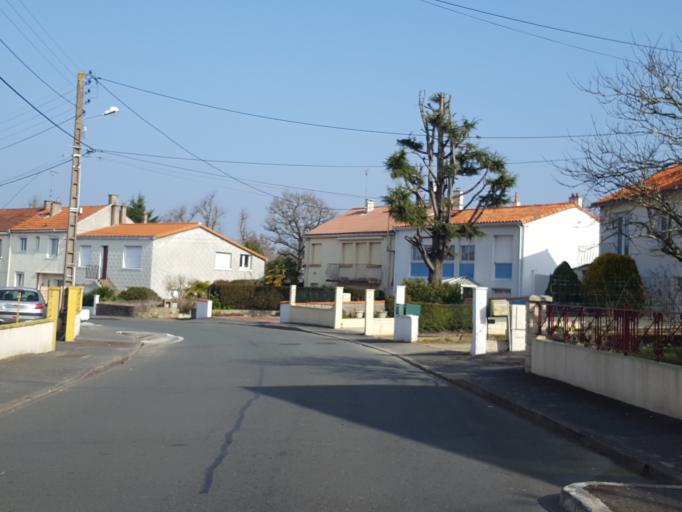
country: FR
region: Pays de la Loire
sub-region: Departement de la Vendee
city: La Roche-sur-Yon
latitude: 46.6681
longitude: -1.4509
